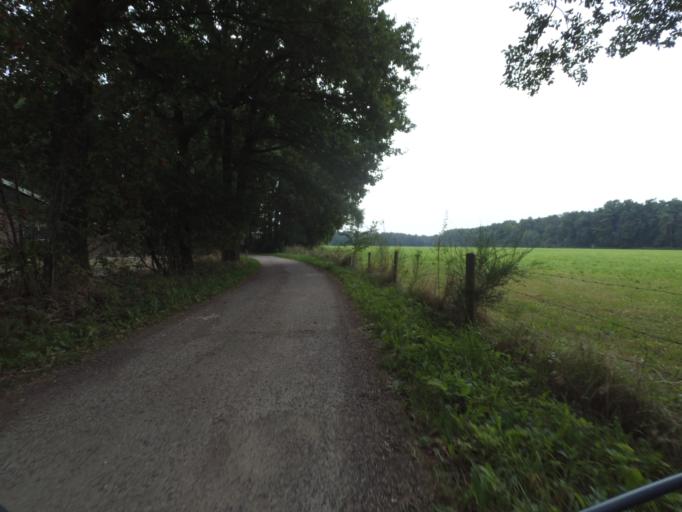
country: NL
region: Overijssel
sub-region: Gemeente Losser
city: Losser
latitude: 52.3071
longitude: 6.9983
